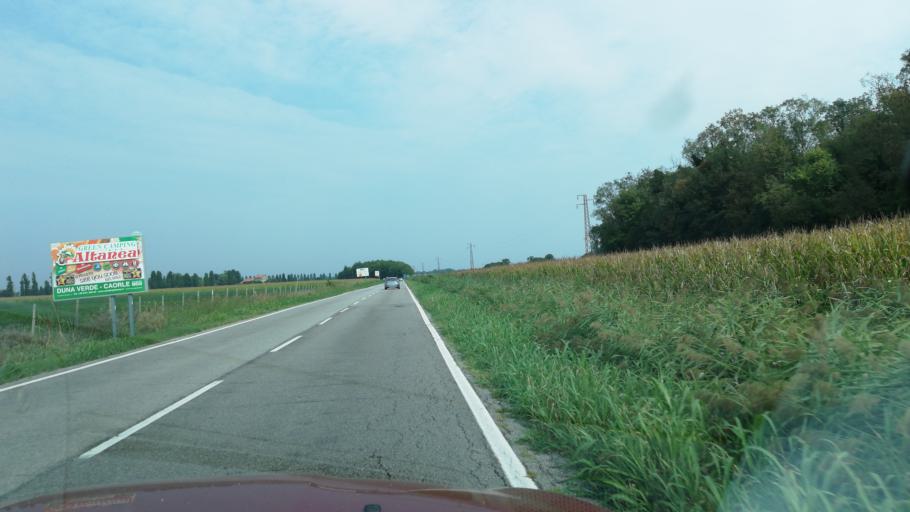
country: IT
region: Veneto
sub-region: Provincia di Venezia
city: La Salute di Livenza
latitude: 45.6139
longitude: 12.8024
